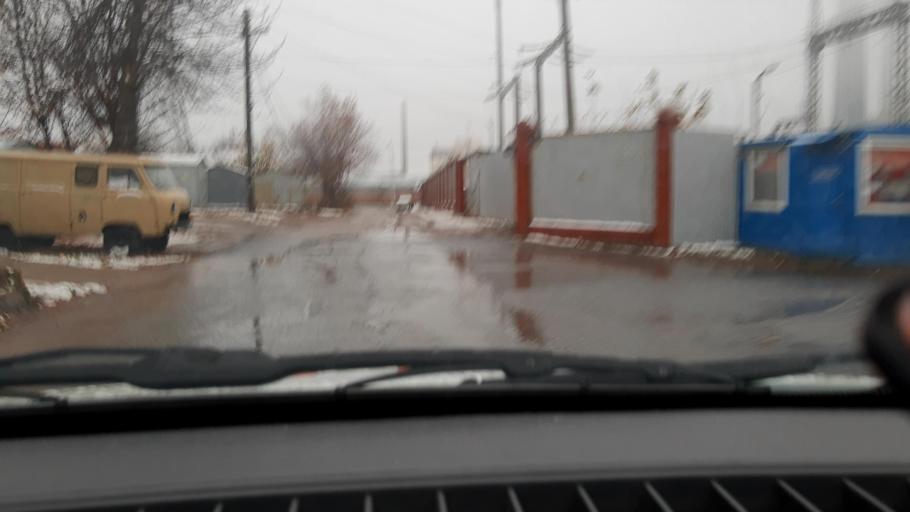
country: RU
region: Bashkortostan
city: Ufa
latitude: 54.7227
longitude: 55.9219
